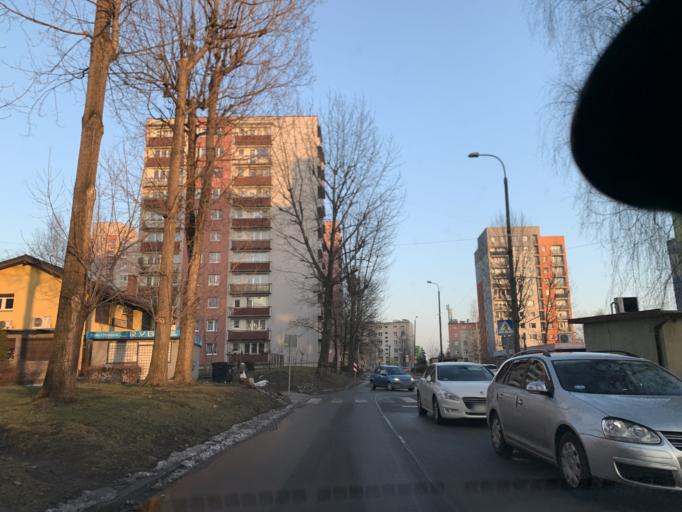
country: PL
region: Silesian Voivodeship
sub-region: Bytom
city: Bytom
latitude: 50.3390
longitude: 18.8912
